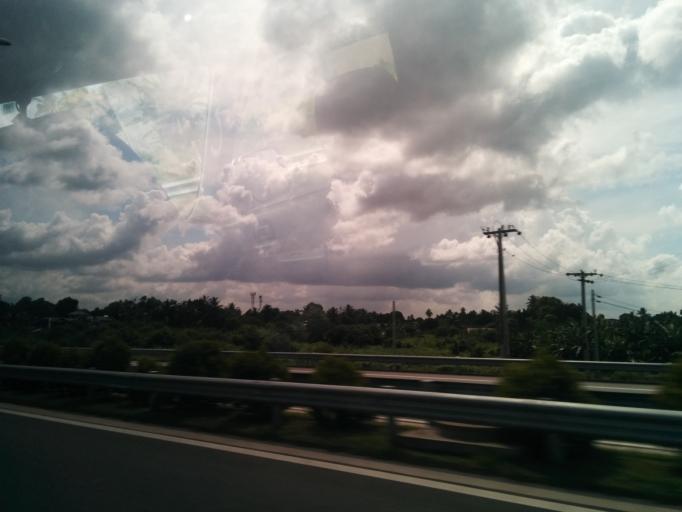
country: LK
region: Western
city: Wattala
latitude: 6.9714
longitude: 79.8939
